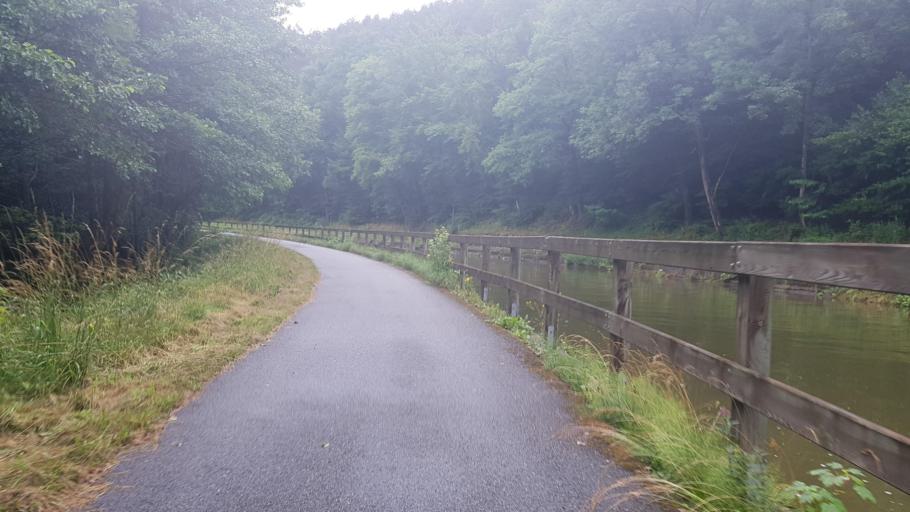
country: FR
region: Lorraine
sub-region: Departement de la Moselle
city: Phalsbourg
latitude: 48.7280
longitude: 7.2988
